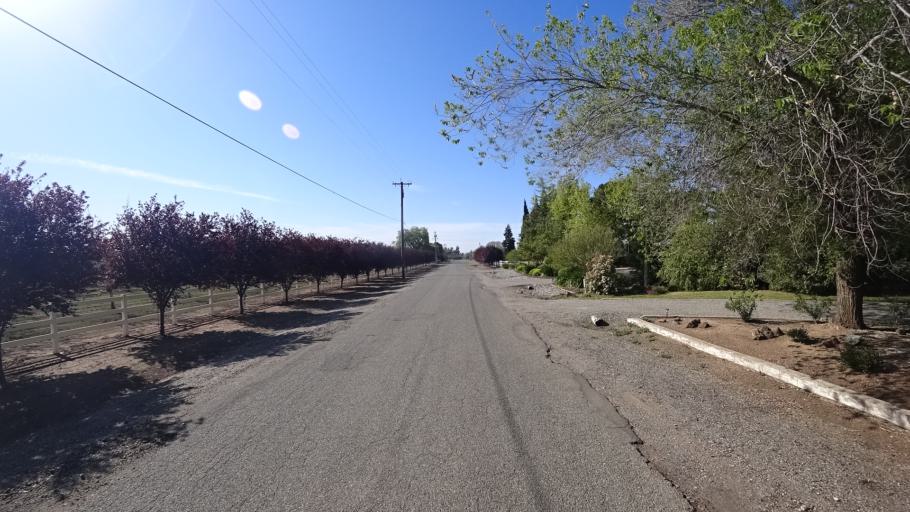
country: US
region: California
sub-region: Glenn County
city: Willows
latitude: 39.5437
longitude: -122.1982
